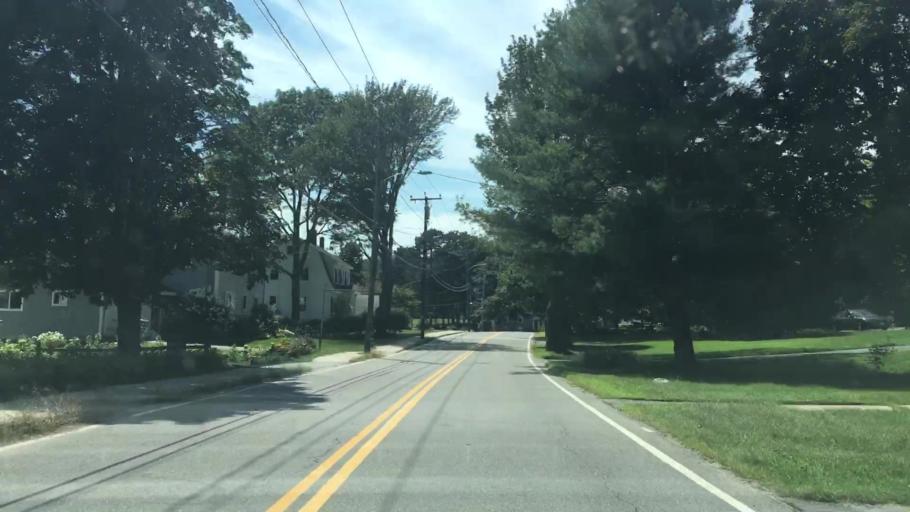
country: US
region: Maine
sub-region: Cumberland County
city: South Portland
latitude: 43.6239
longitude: -70.2515
